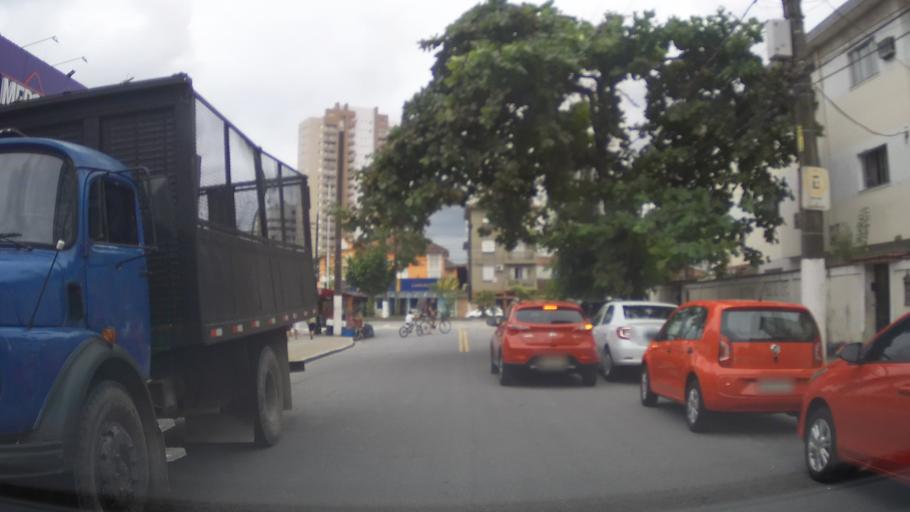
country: BR
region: Sao Paulo
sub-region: Santos
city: Santos
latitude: -23.9643
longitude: -46.3131
